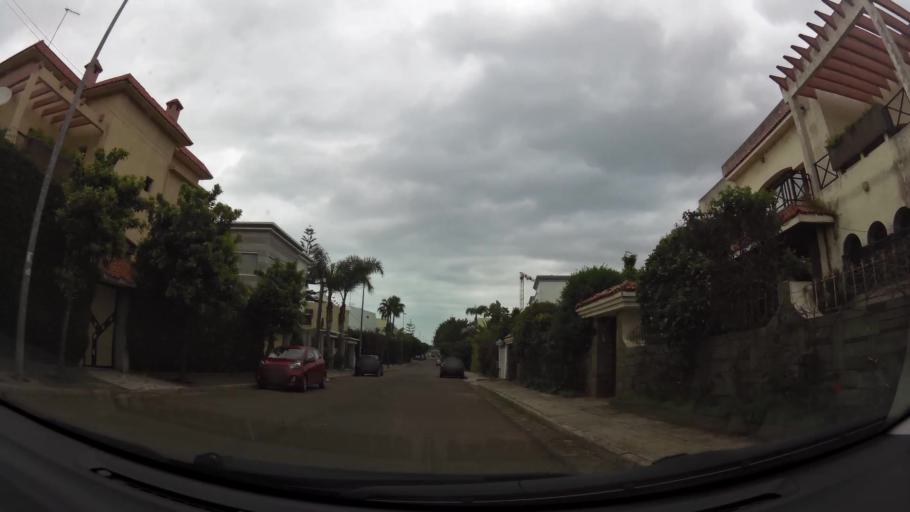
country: MA
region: Grand Casablanca
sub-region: Casablanca
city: Casablanca
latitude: 33.5692
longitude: -7.6567
